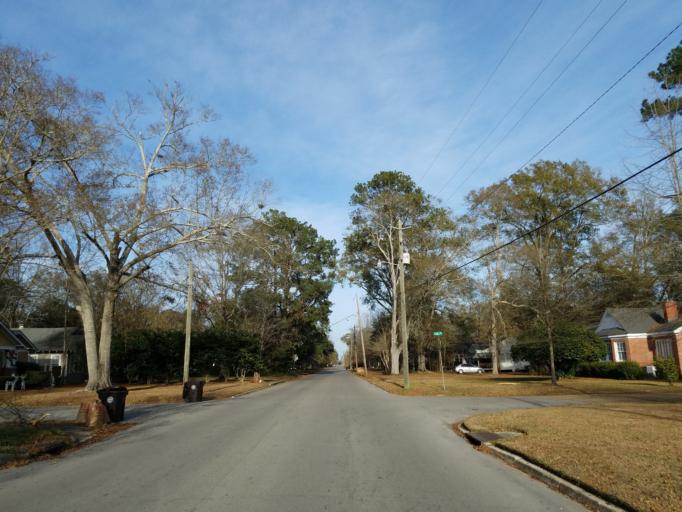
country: US
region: Mississippi
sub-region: Forrest County
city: Hattiesburg
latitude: 31.3179
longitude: -89.3051
